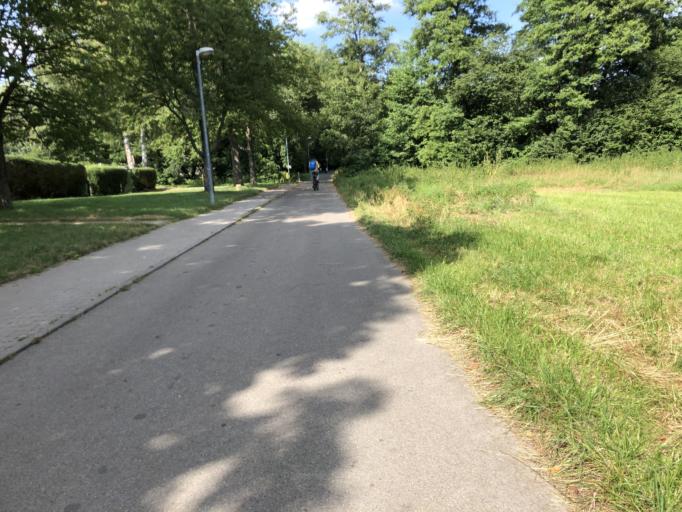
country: DE
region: Baden-Wuerttemberg
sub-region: Regierungsbezirk Stuttgart
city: Sindelfingen
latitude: 48.7227
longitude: 9.0154
